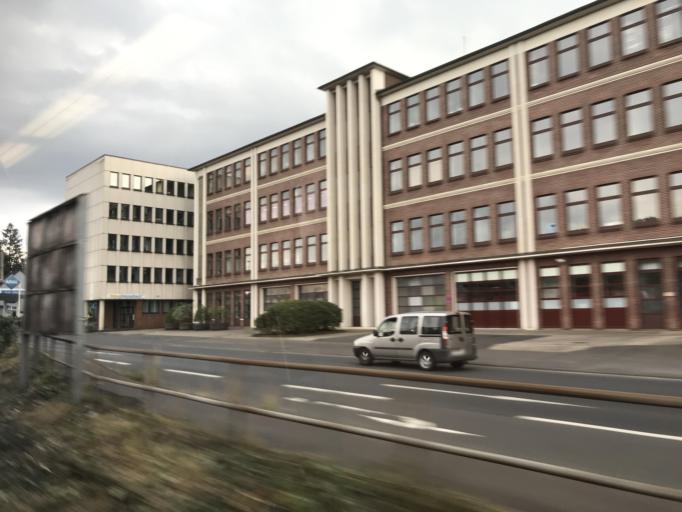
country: DE
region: North Rhine-Westphalia
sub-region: Regierungsbezirk Koln
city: Eitorf
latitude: 50.7743
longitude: 7.4434
